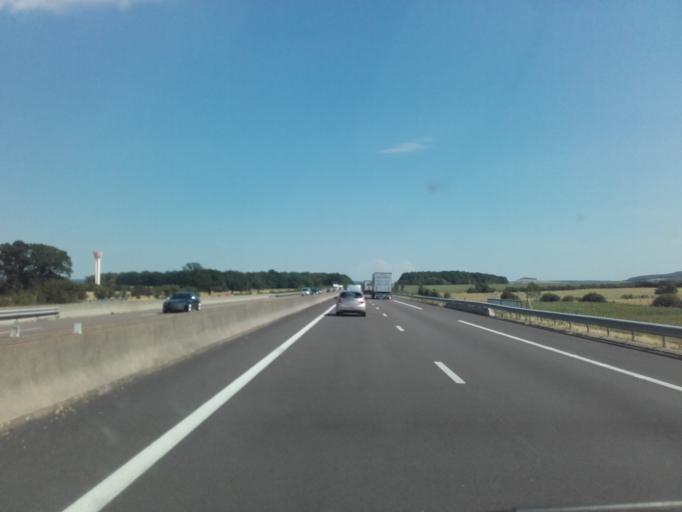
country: FR
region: Bourgogne
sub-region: Departement de la Cote-d'Or
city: Semur-en-Auxois
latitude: 47.3701
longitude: 4.4020
